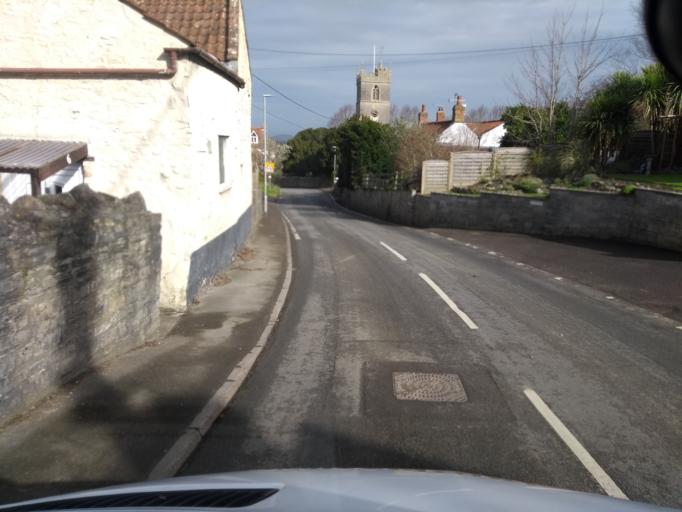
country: GB
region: England
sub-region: Somerset
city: Woolavington
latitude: 51.1694
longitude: -2.9343
